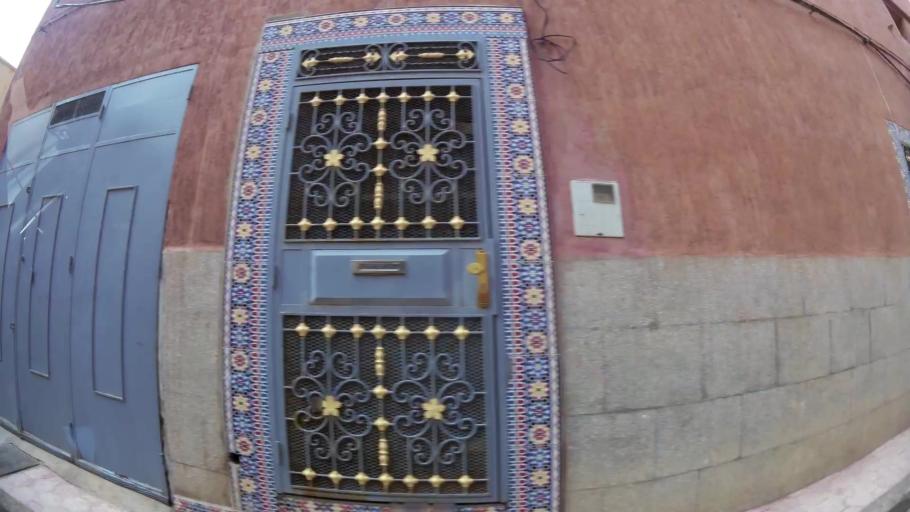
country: MA
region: Oriental
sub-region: Oujda-Angad
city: Oujda
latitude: 34.6840
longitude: -1.9077
